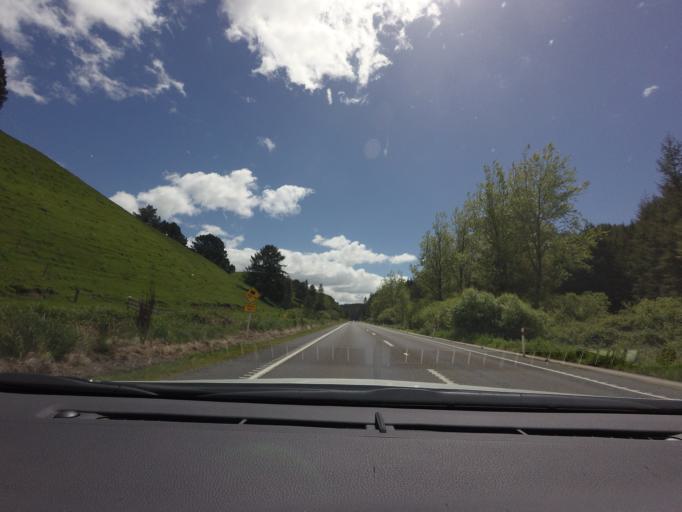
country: NZ
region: Bay of Plenty
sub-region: Rotorua District
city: Rotorua
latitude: -38.2178
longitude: 176.2785
